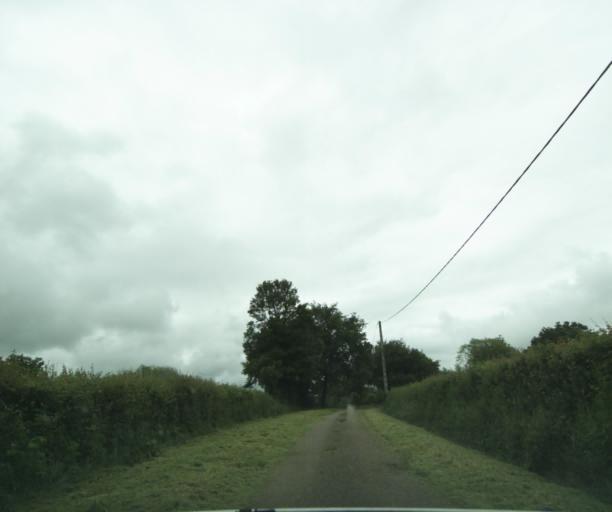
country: FR
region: Bourgogne
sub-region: Departement de Saone-et-Loire
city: Charolles
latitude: 46.4639
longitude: 4.3525
